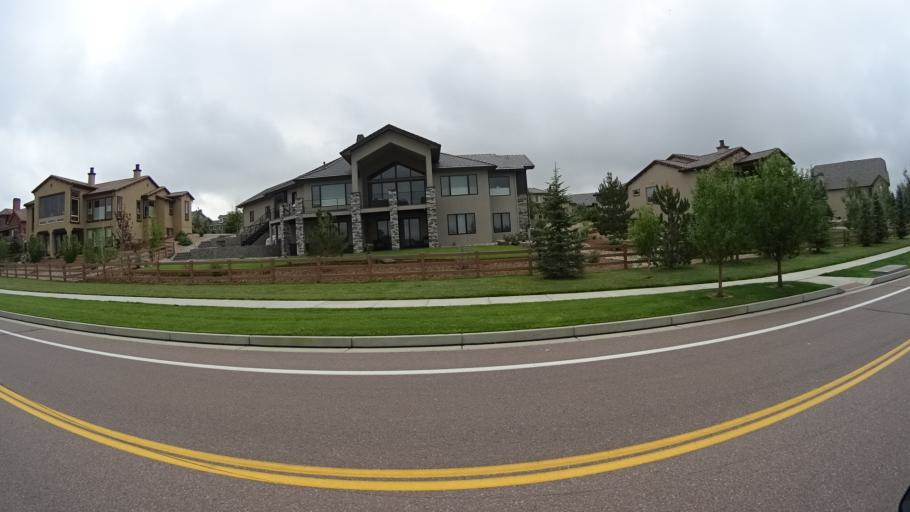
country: US
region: Colorado
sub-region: El Paso County
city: Gleneagle
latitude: 39.0286
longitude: -104.7899
